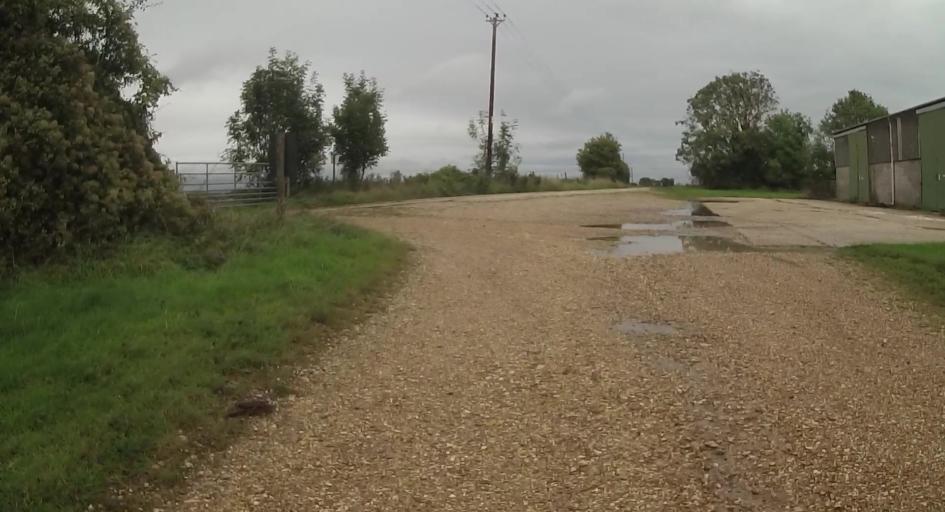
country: GB
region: England
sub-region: Hampshire
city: Basingstoke
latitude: 51.2731
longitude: -1.1360
